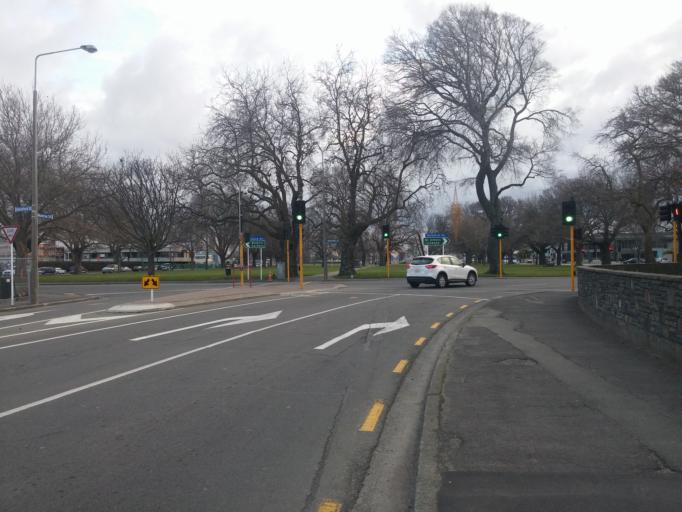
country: NZ
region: Canterbury
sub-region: Christchurch City
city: Christchurch
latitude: -43.5322
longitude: 172.6428
